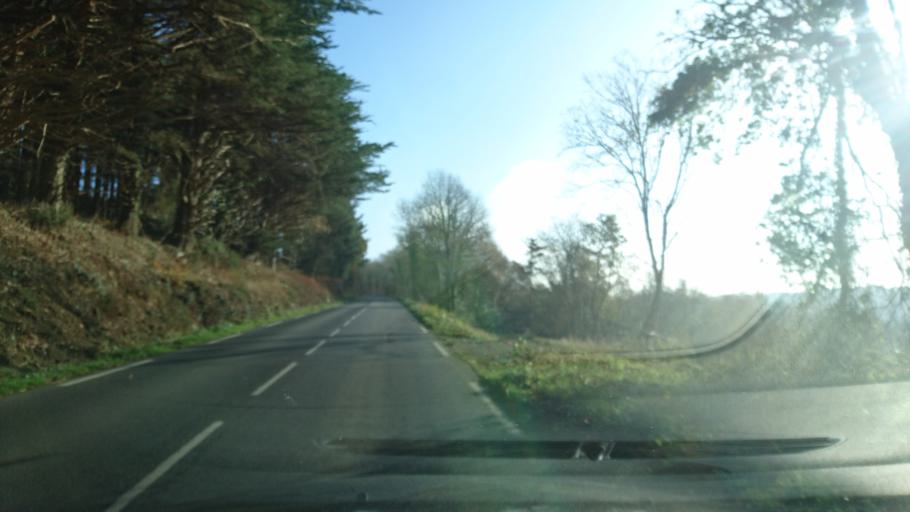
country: FR
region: Brittany
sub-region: Departement du Finistere
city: Logonna-Daoulas
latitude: 48.2760
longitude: -4.2728
